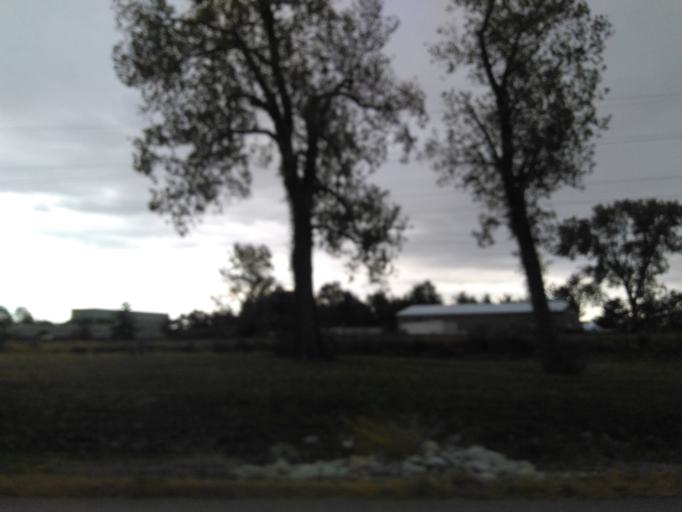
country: US
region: Illinois
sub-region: Madison County
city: Highland
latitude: 38.7400
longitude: -89.6962
